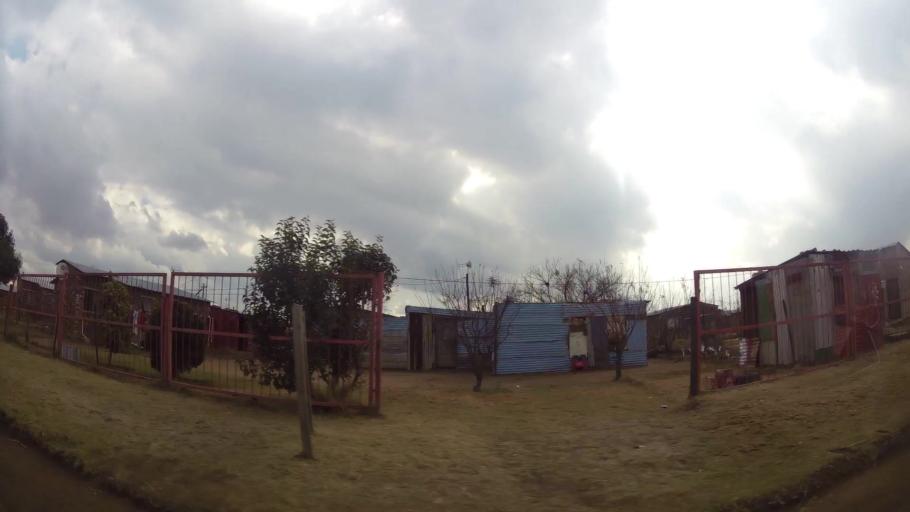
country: ZA
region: Orange Free State
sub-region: Fezile Dabi District Municipality
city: Sasolburg
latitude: -26.8622
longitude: 27.9014
